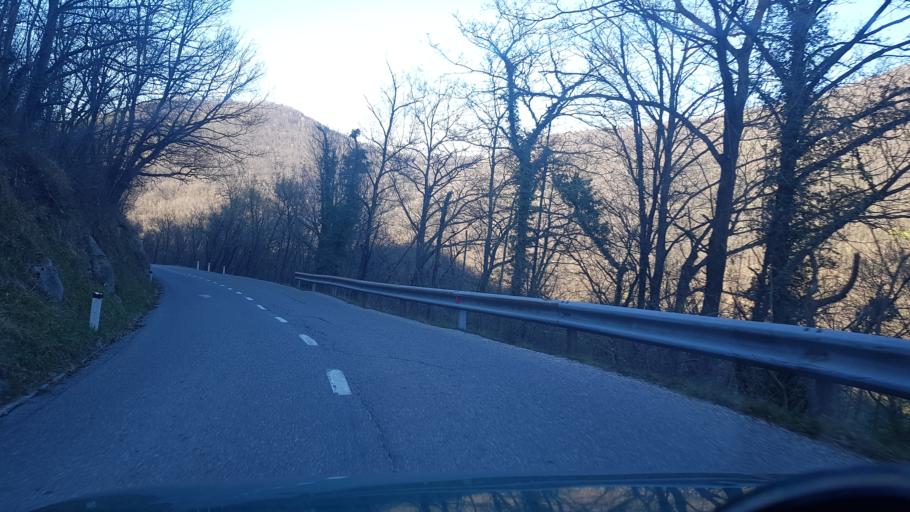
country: SI
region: Kanal
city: Deskle
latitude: 46.0300
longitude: 13.5919
